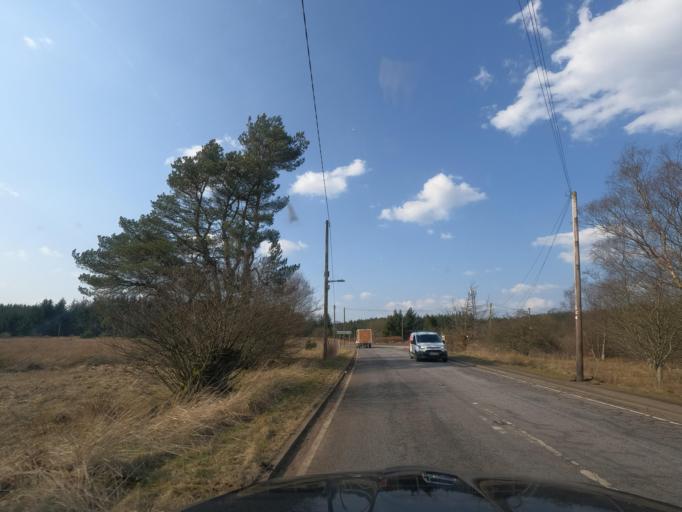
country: GB
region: Scotland
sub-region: South Lanarkshire
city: Forth
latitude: 55.7748
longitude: -3.6777
